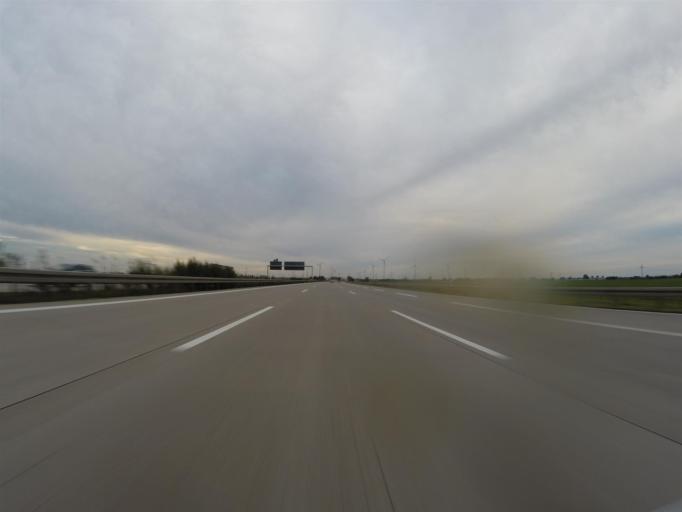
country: DE
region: Saxony-Anhalt
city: Nessa
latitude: 51.1734
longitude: 12.0006
